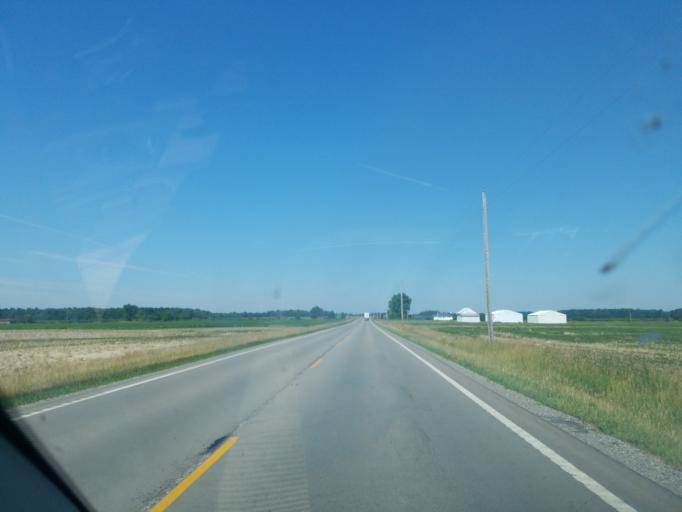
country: US
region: Ohio
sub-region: Shelby County
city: Jackson Center
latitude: 40.4393
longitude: -83.9871
